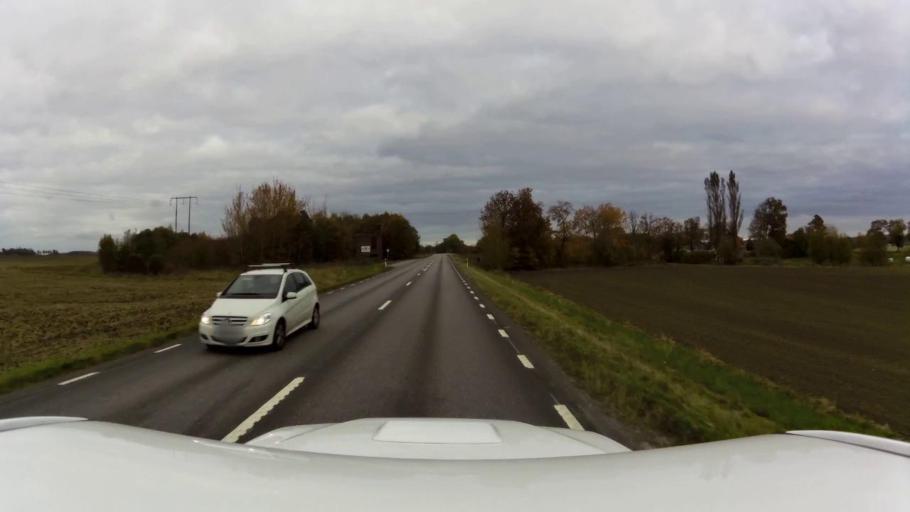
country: SE
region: OEstergoetland
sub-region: Linkopings Kommun
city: Ljungsbro
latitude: 58.5138
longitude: 15.4403
